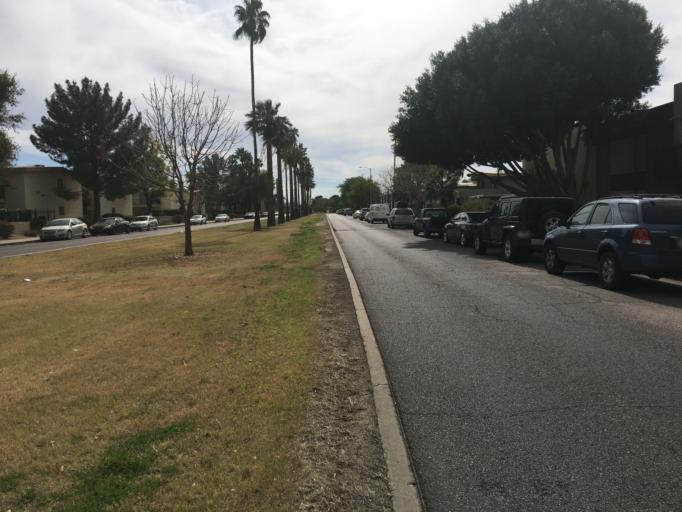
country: US
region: Arizona
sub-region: Maricopa County
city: Phoenix
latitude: 33.5338
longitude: -112.0956
